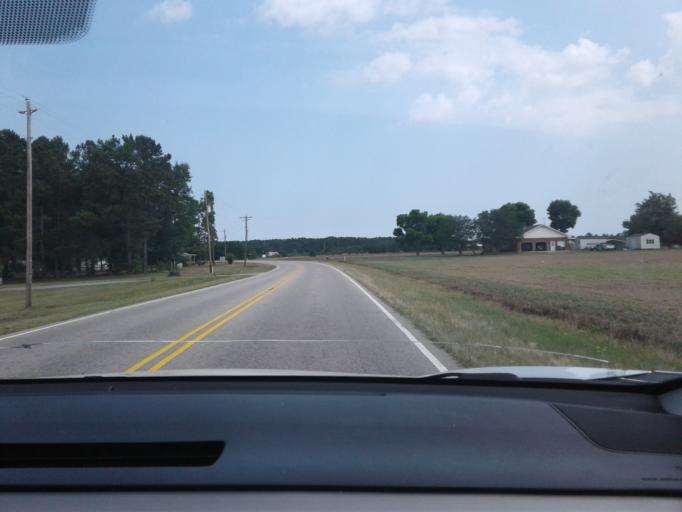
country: US
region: North Carolina
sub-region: Harnett County
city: Coats
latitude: 35.3845
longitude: -78.6639
